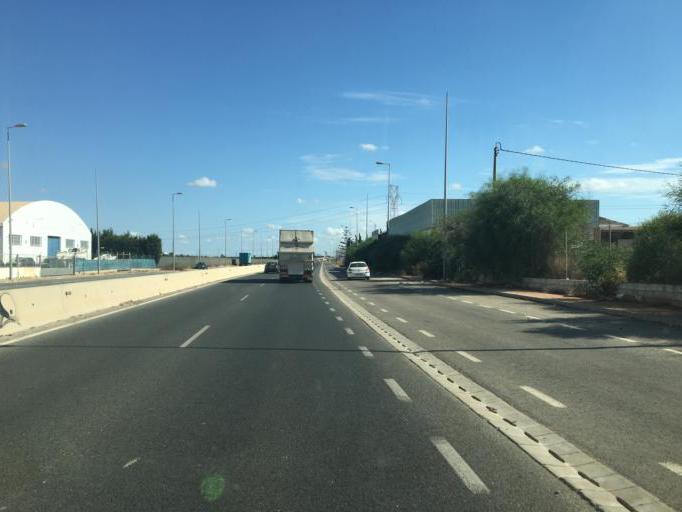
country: ES
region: Murcia
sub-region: Murcia
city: Cartagena
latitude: 37.6489
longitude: -0.9846
